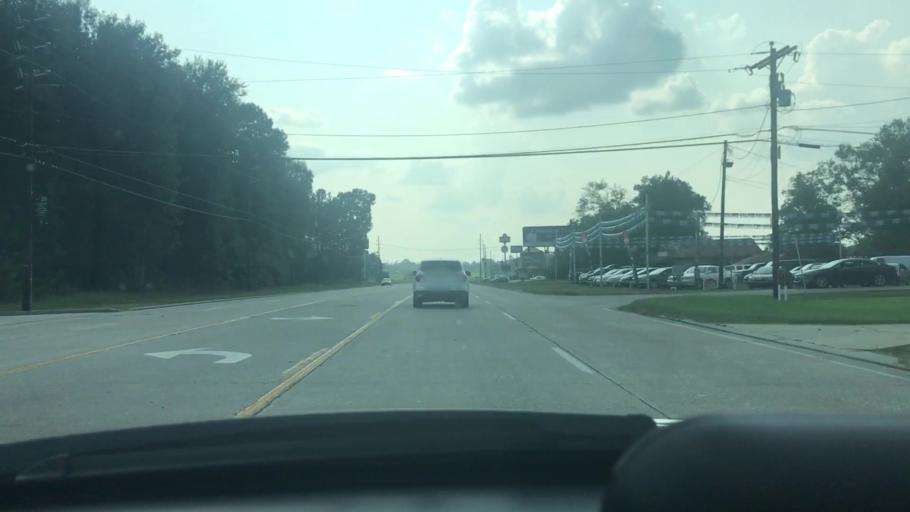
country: US
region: Louisiana
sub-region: Tangipahoa Parish
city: Natalbany
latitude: 30.5192
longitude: -90.4950
